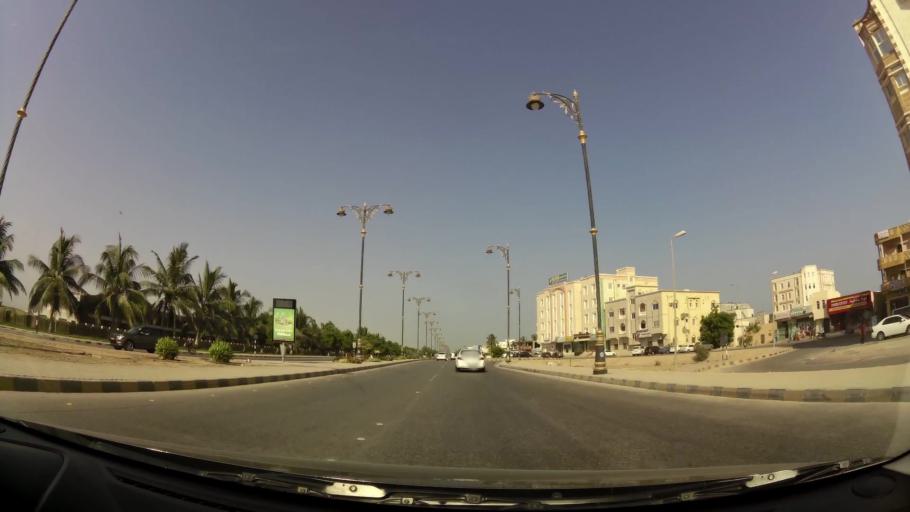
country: OM
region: Zufar
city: Salalah
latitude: 17.0046
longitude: 54.0413
